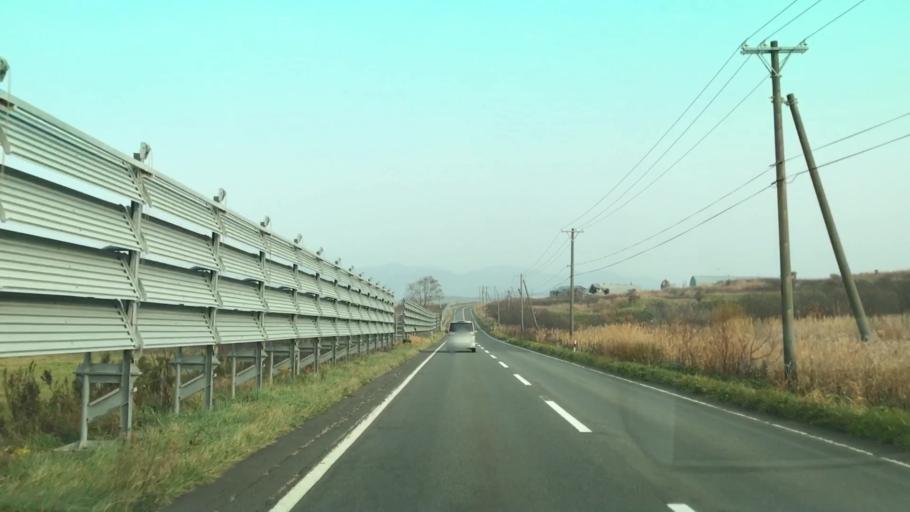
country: JP
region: Hokkaido
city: Ishikari
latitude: 43.3457
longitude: 141.4240
